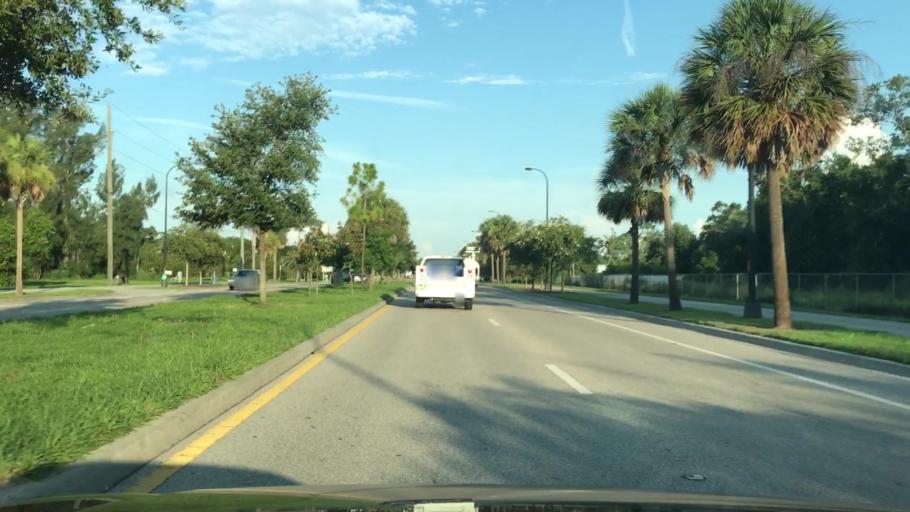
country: US
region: Florida
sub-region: Sarasota County
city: Fruitville
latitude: 27.3383
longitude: -82.4098
